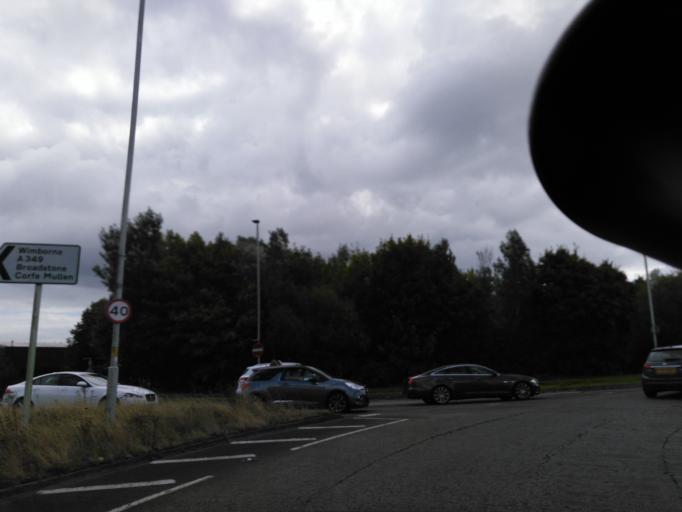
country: GB
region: England
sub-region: Poole
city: Poole
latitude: 50.7325
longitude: -1.9909
